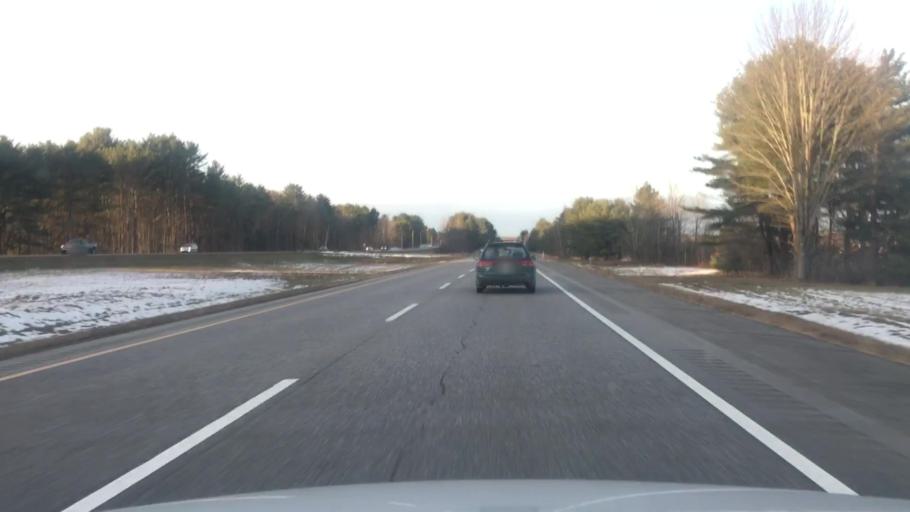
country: US
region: Maine
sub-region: Kennebec County
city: Vassalboro
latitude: 44.4969
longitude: -69.7043
